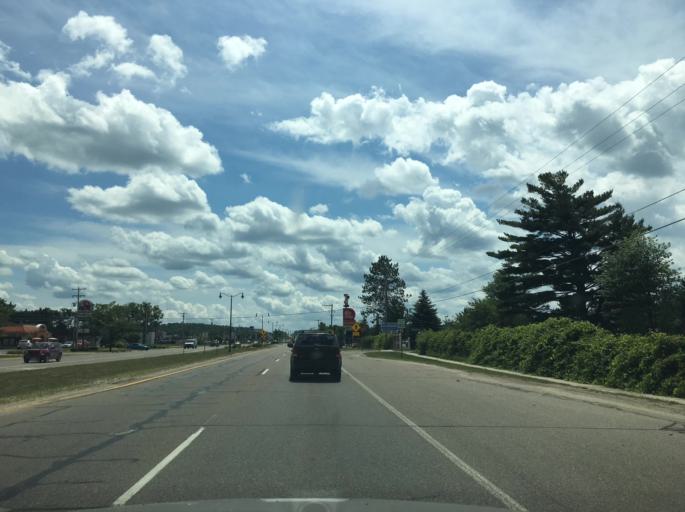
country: US
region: Michigan
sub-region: Crawford County
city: Grayling
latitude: 44.6552
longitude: -84.7085
